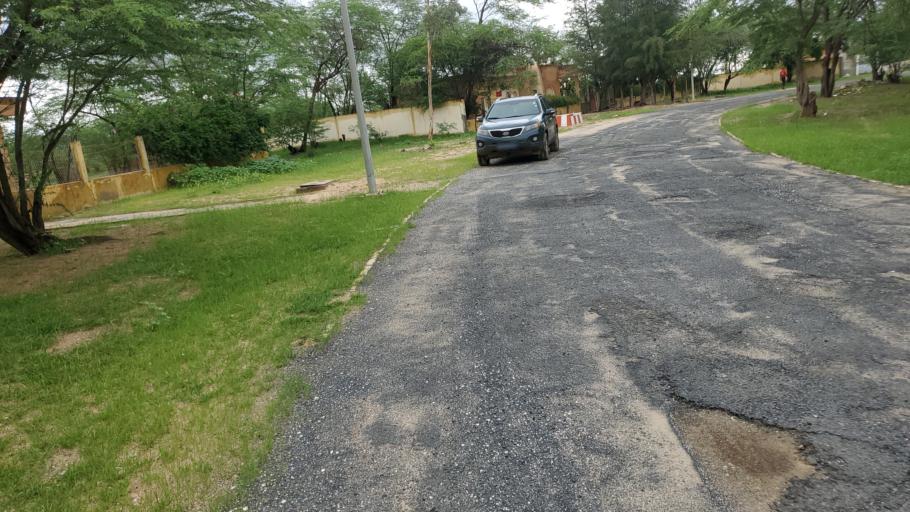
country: SN
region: Saint-Louis
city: Saint-Louis
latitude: 16.0699
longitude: -16.4197
